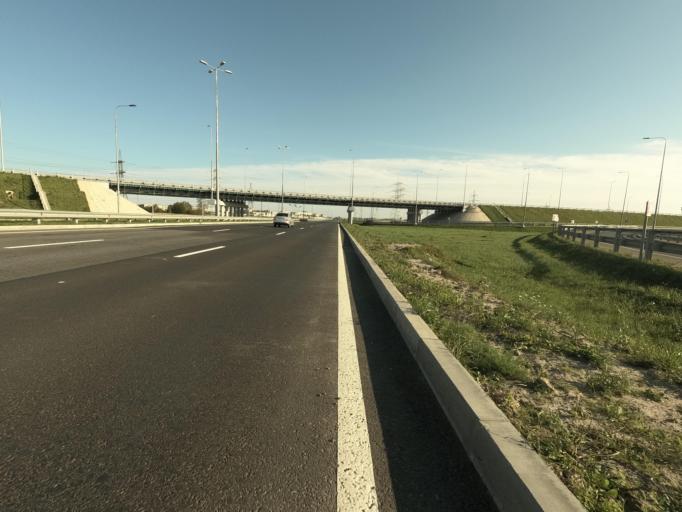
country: RU
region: St.-Petersburg
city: Kolpino
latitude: 59.7439
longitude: 30.5398
